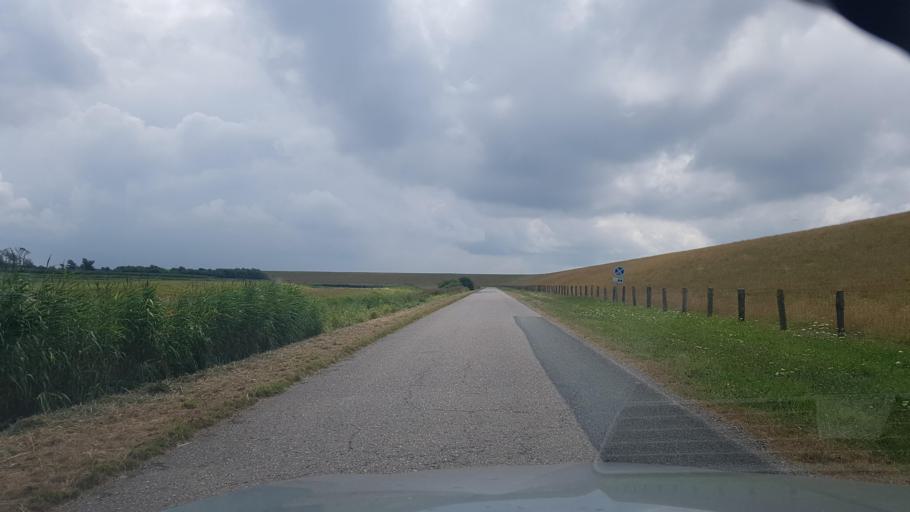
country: DE
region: Schleswig-Holstein
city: Elisabeth-Sophien-Koog
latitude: 54.4937
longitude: 8.8084
